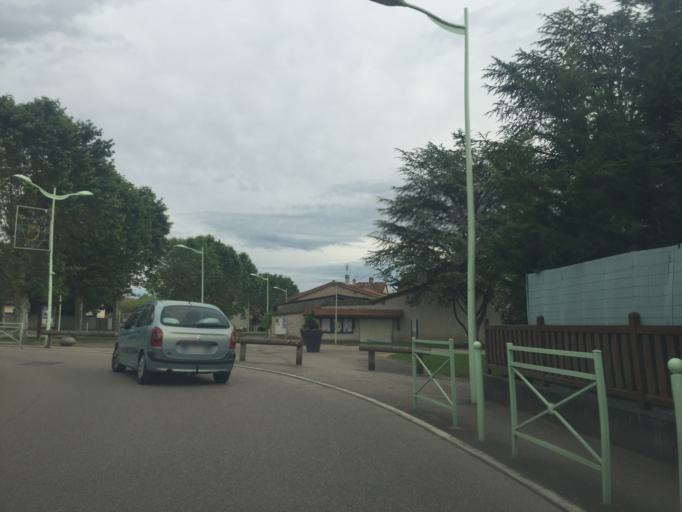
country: FR
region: Rhone-Alpes
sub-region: Departement de l'Ain
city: Thil
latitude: 45.8146
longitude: 5.0214
